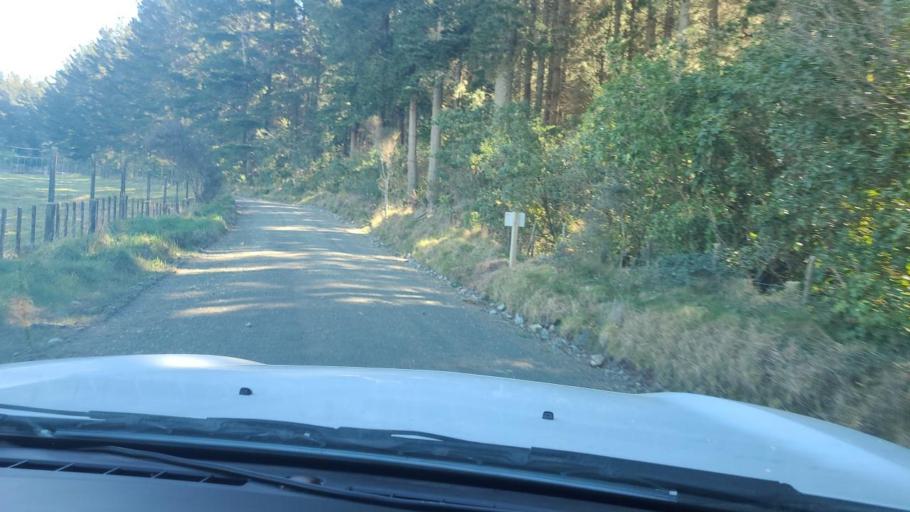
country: NZ
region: Hawke's Bay
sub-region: Napier City
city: Taradale
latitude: -39.4146
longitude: 176.4671
